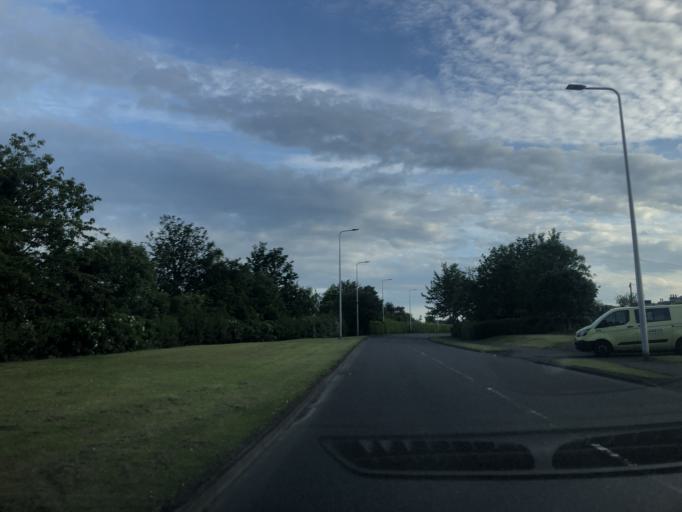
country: GB
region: Scotland
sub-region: Fife
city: Leven
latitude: 56.1884
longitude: -3.0043
